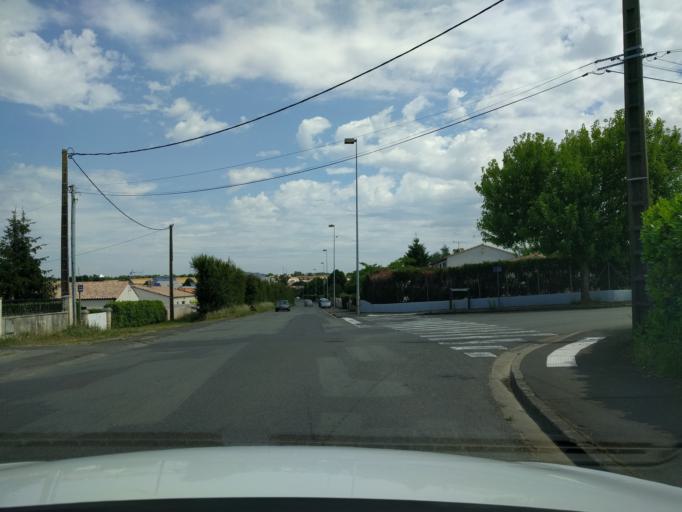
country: FR
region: Poitou-Charentes
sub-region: Departement des Deux-Sevres
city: Niort
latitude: 46.3439
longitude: -0.4856
